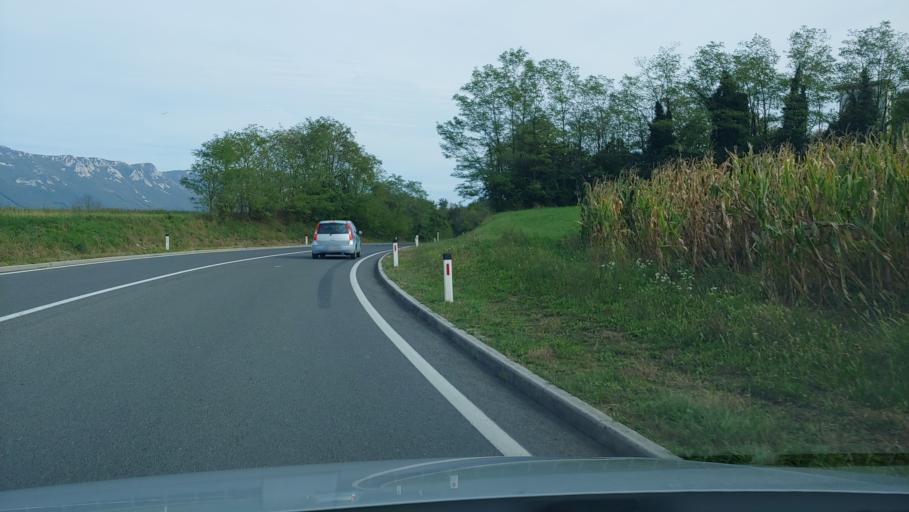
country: SI
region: Ajdovscina
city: Lokavec
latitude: 45.8866
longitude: 13.8474
